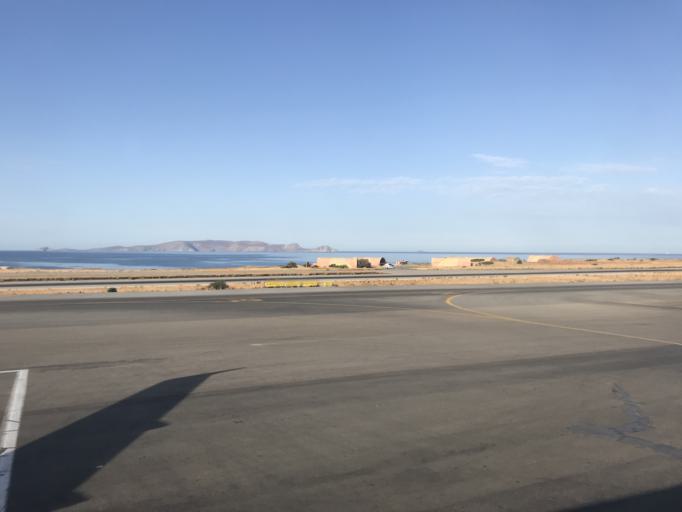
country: GR
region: Crete
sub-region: Nomos Irakleiou
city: Nea Alikarnassos
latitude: 35.3385
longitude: 25.1775
